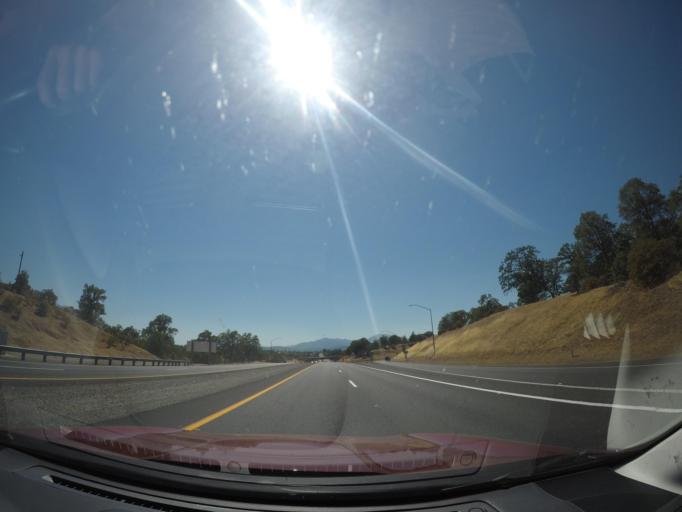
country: US
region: California
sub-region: Shasta County
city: Redding
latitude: 40.6132
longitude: -122.3586
